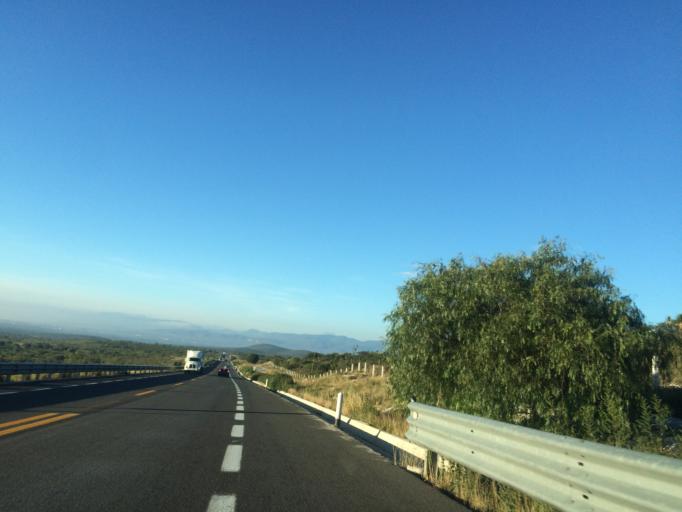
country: MX
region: Puebla
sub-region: Tehuacan
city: Magdalena Cuayucatepec
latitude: 18.6128
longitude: -97.4759
